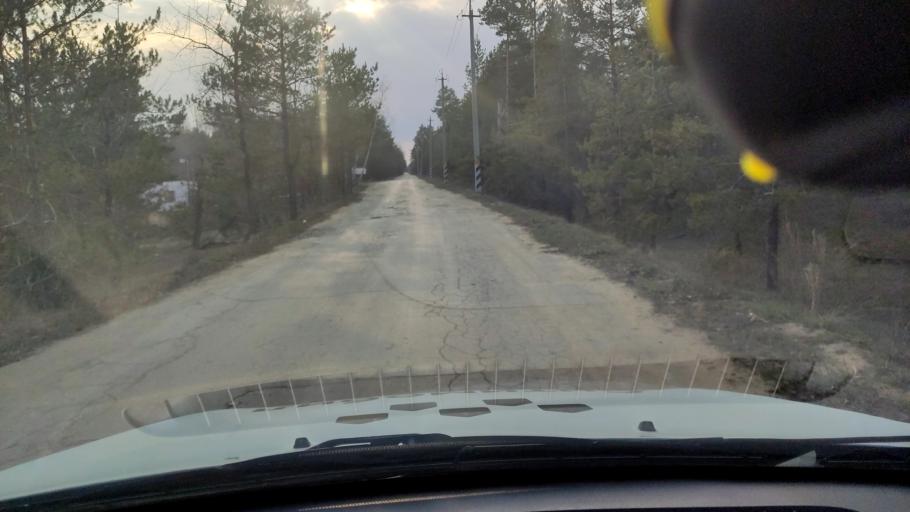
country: RU
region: Samara
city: Zhigulevsk
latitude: 53.4586
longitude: 49.6184
